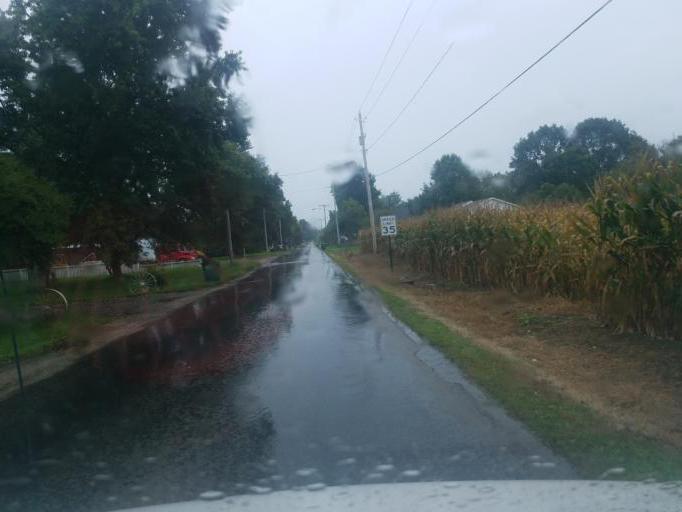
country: US
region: Ohio
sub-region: Wayne County
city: Creston
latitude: 40.9860
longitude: -81.8894
